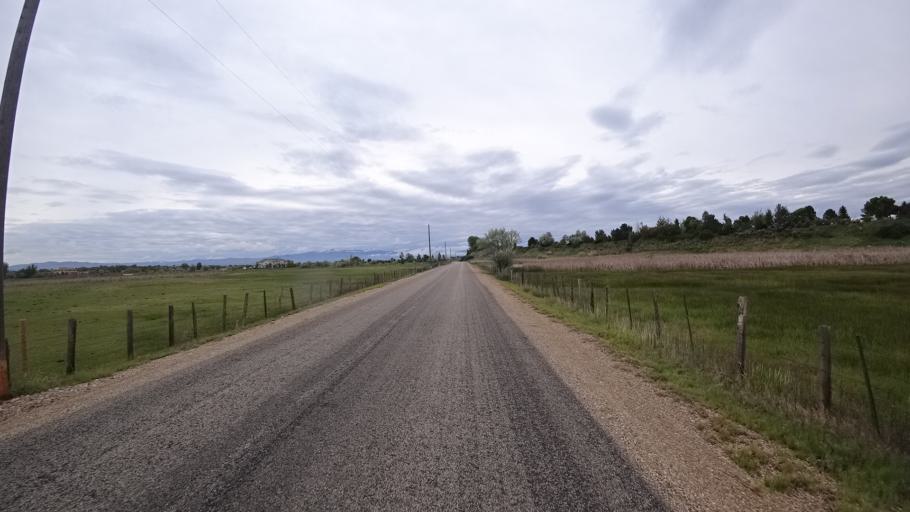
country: US
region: Idaho
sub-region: Ada County
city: Star
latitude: 43.6704
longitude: -116.4822
